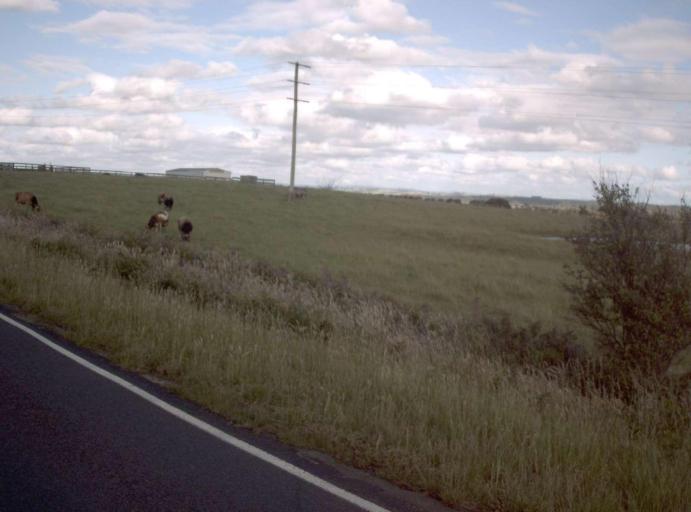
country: AU
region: Victoria
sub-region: Bass Coast
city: North Wonthaggi
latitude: -38.5362
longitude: 145.8693
